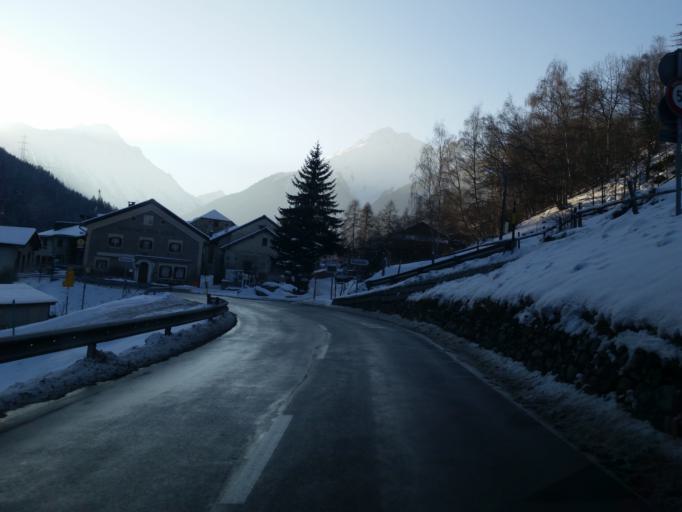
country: CH
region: Grisons
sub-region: Inn District
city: Zernez
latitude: 46.7703
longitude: 10.1451
